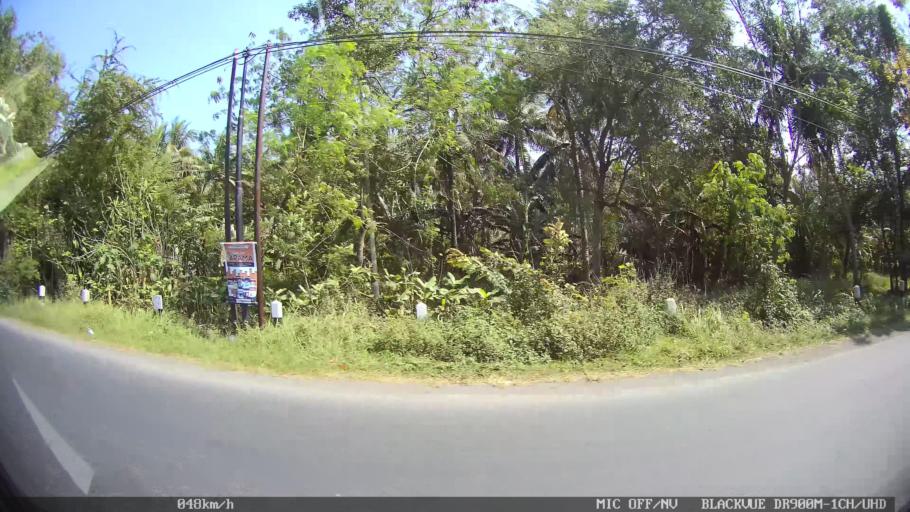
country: ID
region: Daerah Istimewa Yogyakarta
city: Srandakan
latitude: -7.9471
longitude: 110.2239
